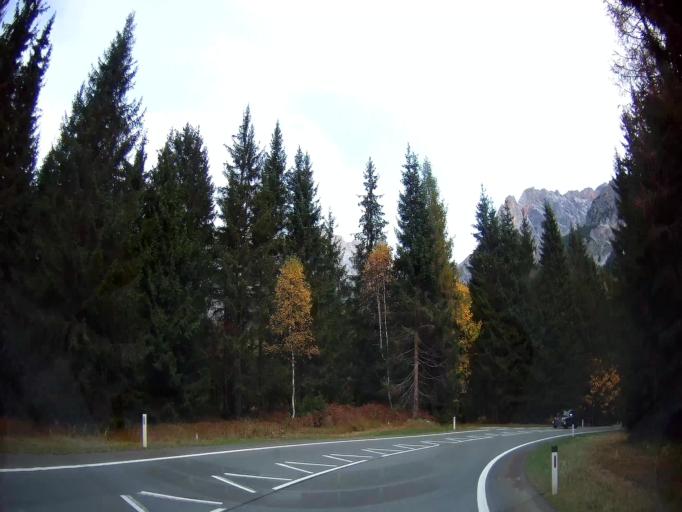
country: AT
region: Salzburg
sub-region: Politischer Bezirk Zell am See
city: Dienten am Hochkonig
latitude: 47.4039
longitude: 12.9839
